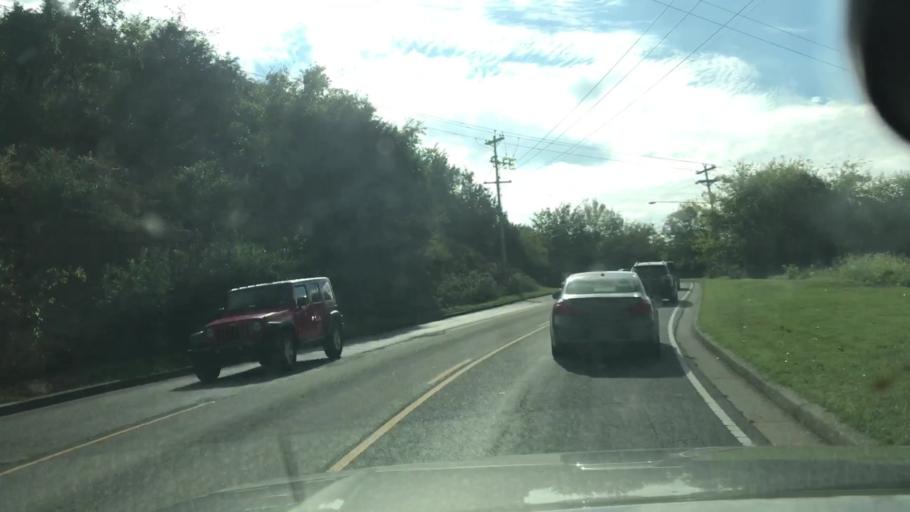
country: US
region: Tennessee
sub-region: Williamson County
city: Franklin
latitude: 35.9234
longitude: -86.8253
